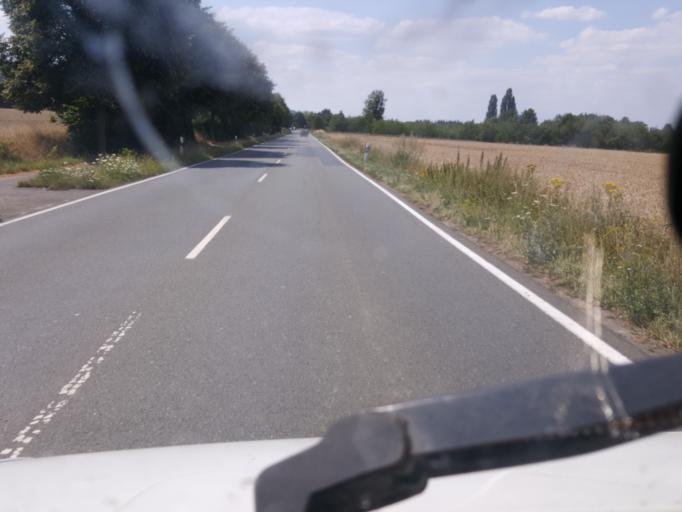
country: DE
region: North Rhine-Westphalia
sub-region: Regierungsbezirk Detmold
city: Minden
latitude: 52.2619
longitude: 8.8627
